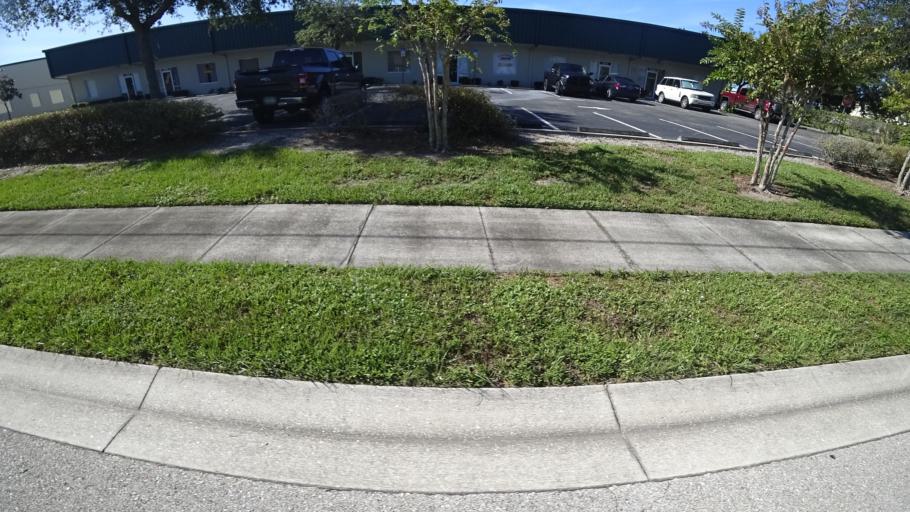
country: US
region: Florida
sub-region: Manatee County
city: Whitfield
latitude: 27.4128
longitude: -82.5359
